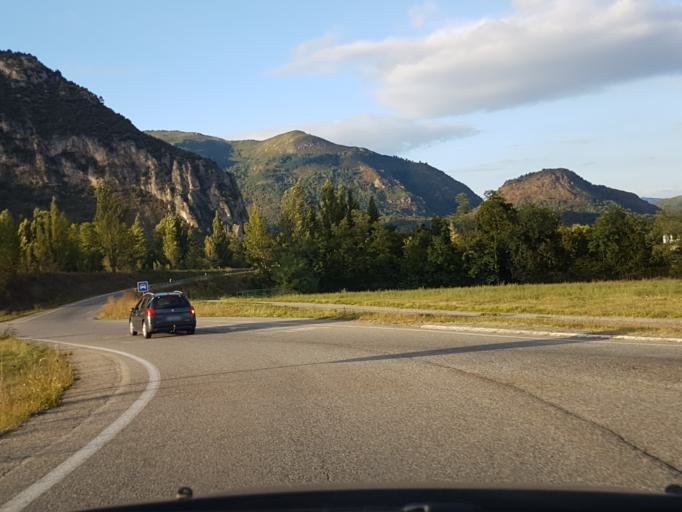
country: FR
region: Midi-Pyrenees
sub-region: Departement de l'Ariege
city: Tarascon-sur-Ariege
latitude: 42.8527
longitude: 1.5917
